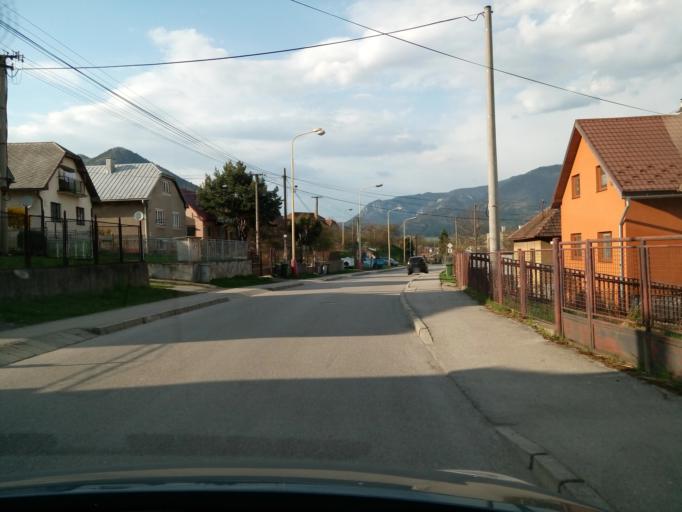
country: SK
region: Zilinsky
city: Ruzomberok
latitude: 49.0730
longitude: 19.2975
